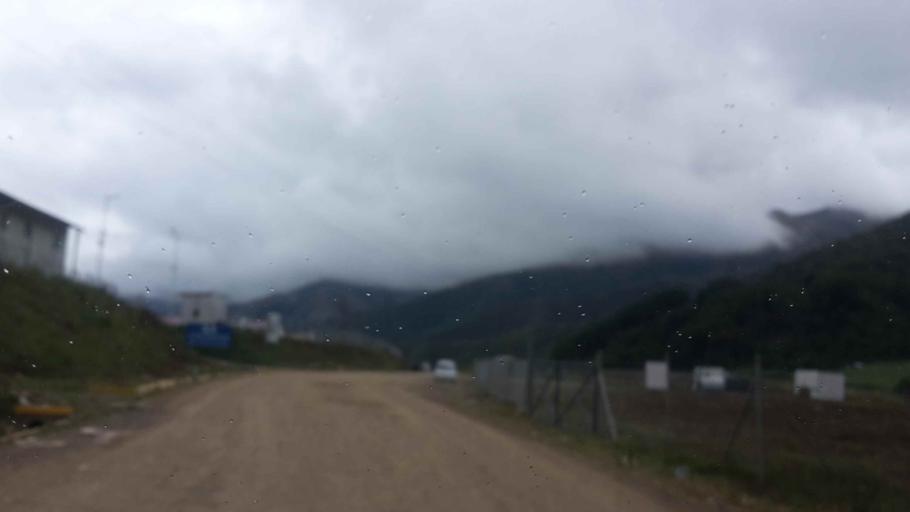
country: BO
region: Cochabamba
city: Totora
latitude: -17.5739
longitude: -65.2849
